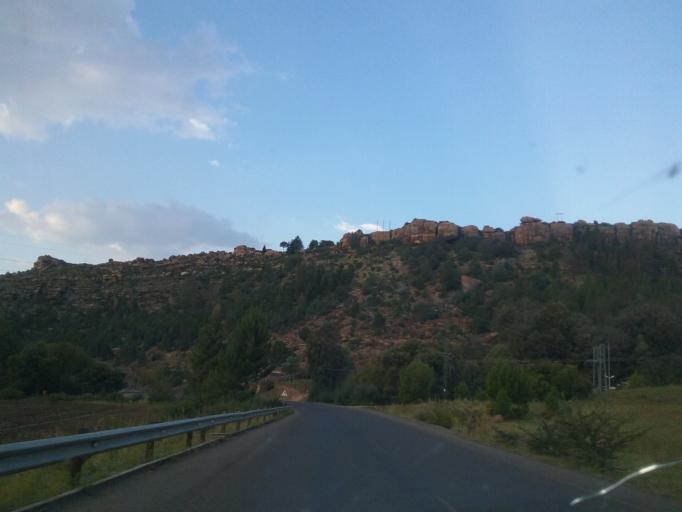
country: LS
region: Quthing
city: Quthing
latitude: -30.4034
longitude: 27.6815
